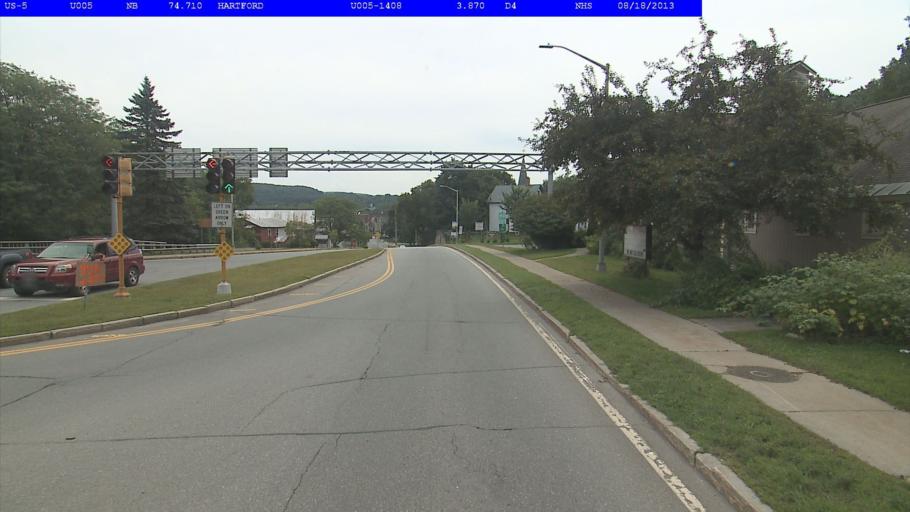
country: US
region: Vermont
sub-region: Windsor County
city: White River Junction
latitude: 43.6508
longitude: -72.3235
